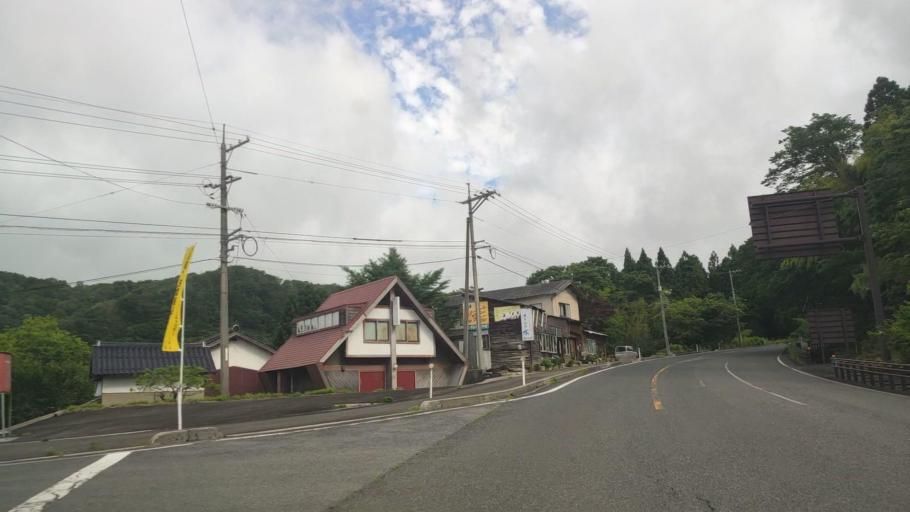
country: JP
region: Tottori
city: Yonago
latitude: 35.3238
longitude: 133.5568
